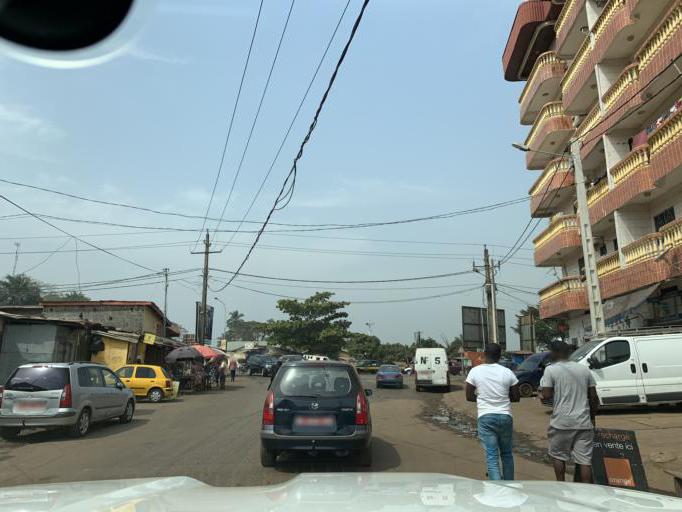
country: GN
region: Conakry
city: Conakry
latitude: 9.5547
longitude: -13.6694
